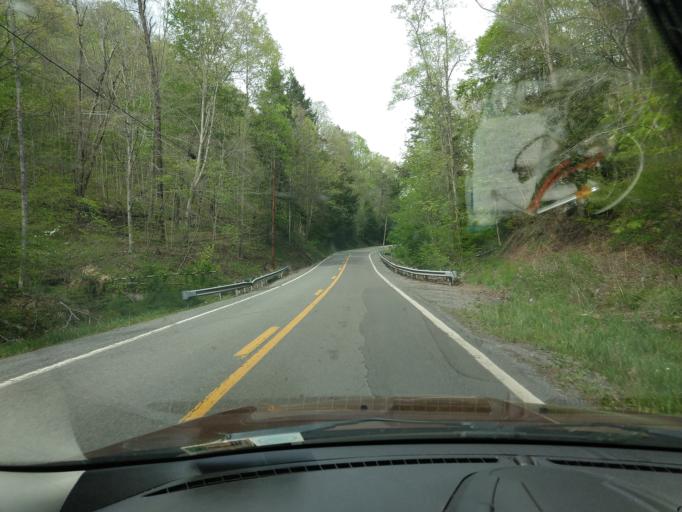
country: US
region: West Virginia
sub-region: McDowell County
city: Welch
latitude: 37.3514
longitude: -81.6657
